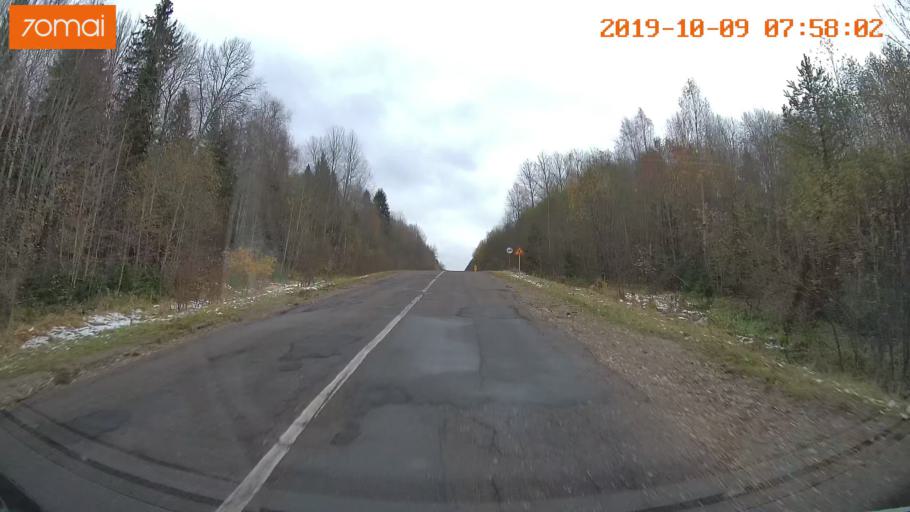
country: RU
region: Jaroslavl
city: Kukoboy
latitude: 58.6970
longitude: 39.9597
